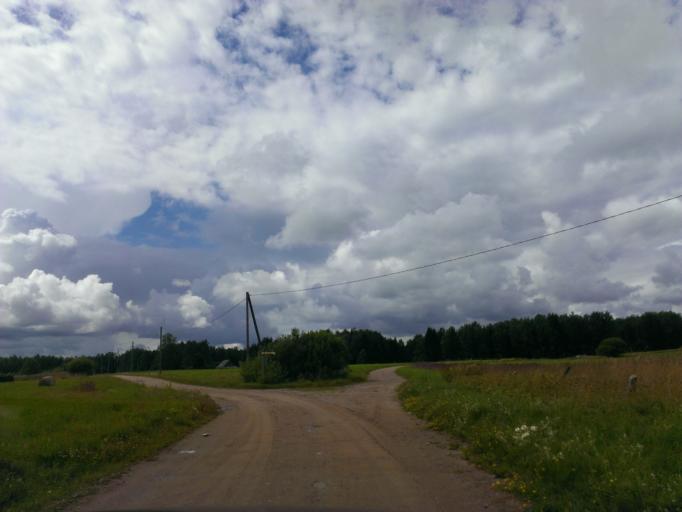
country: LV
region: Ligatne
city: Ligatne
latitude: 57.2265
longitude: 24.9946
